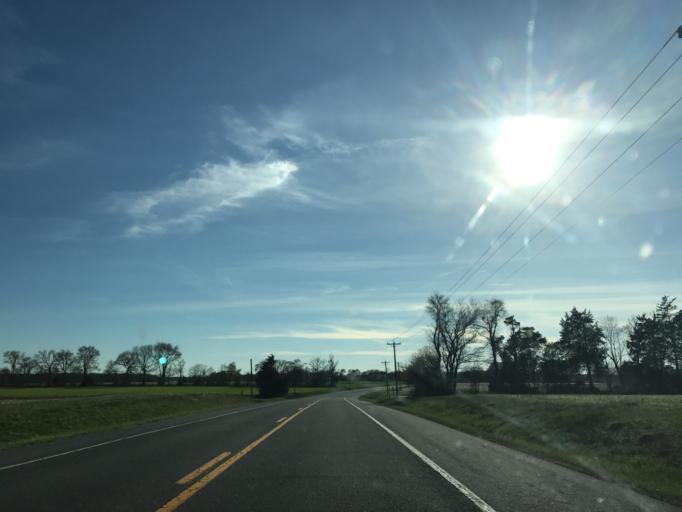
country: US
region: Maryland
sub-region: Caroline County
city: Greensboro
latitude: 39.1391
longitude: -75.7563
